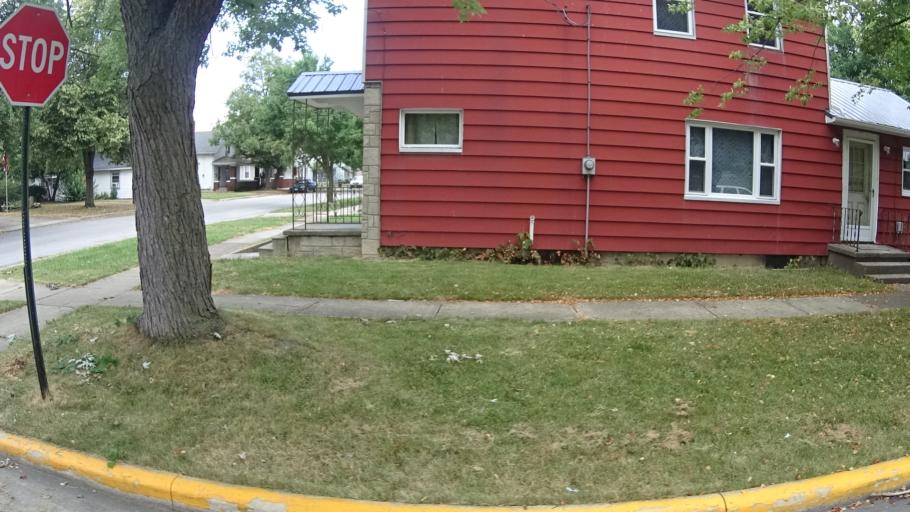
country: US
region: Ohio
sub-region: Erie County
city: Sandusky
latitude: 41.4441
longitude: -82.7229
